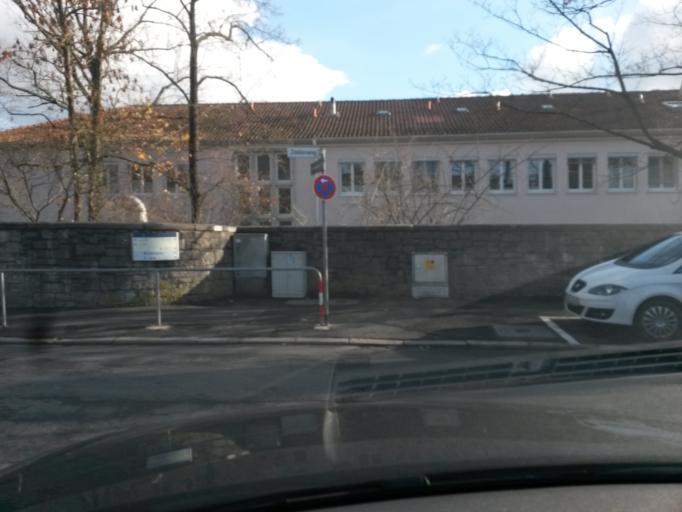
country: DE
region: Bavaria
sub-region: Regierungsbezirk Unterfranken
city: Wuerzburg
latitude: 49.8041
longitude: 9.9578
